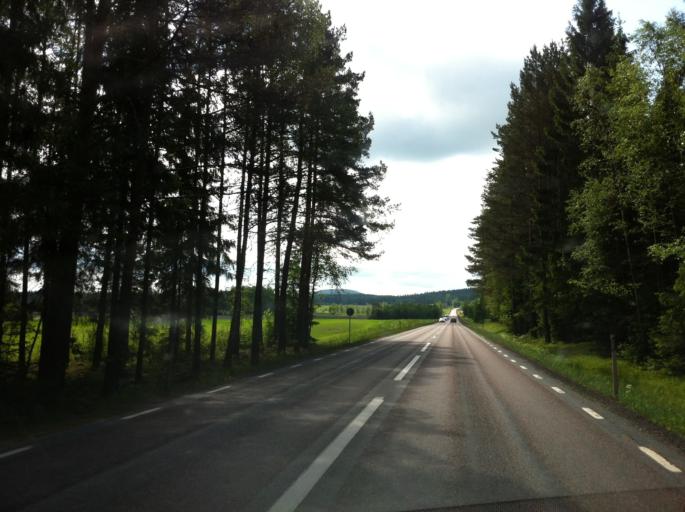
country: SE
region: Vaermland
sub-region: Karlstads Kommun
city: Edsvalla
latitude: 59.6102
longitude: 13.1542
